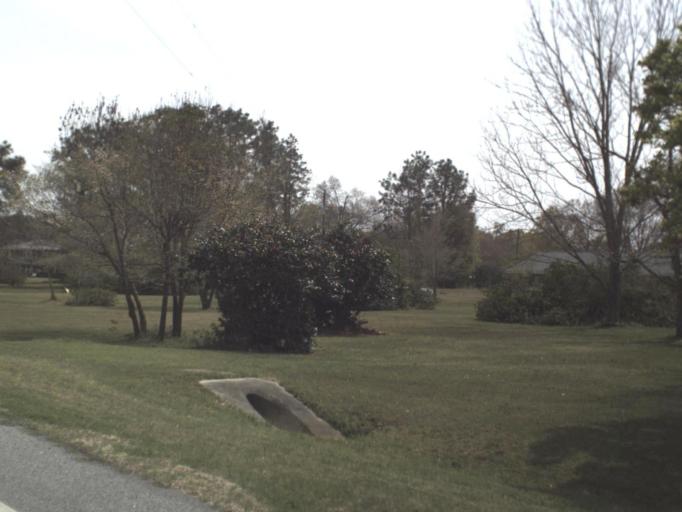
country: US
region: Alabama
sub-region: Geneva County
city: Geneva
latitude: 30.9420
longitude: -85.8194
